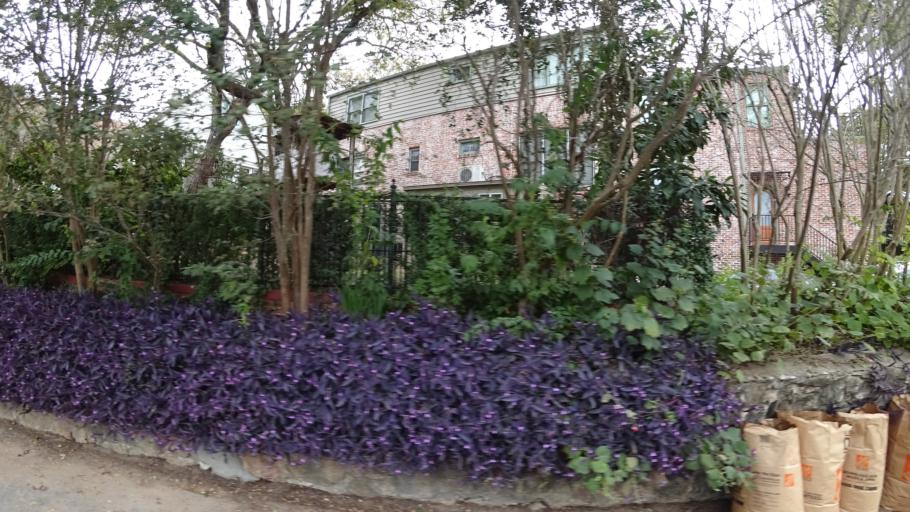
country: US
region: Texas
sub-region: Travis County
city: Austin
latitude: 30.2868
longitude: -97.7553
